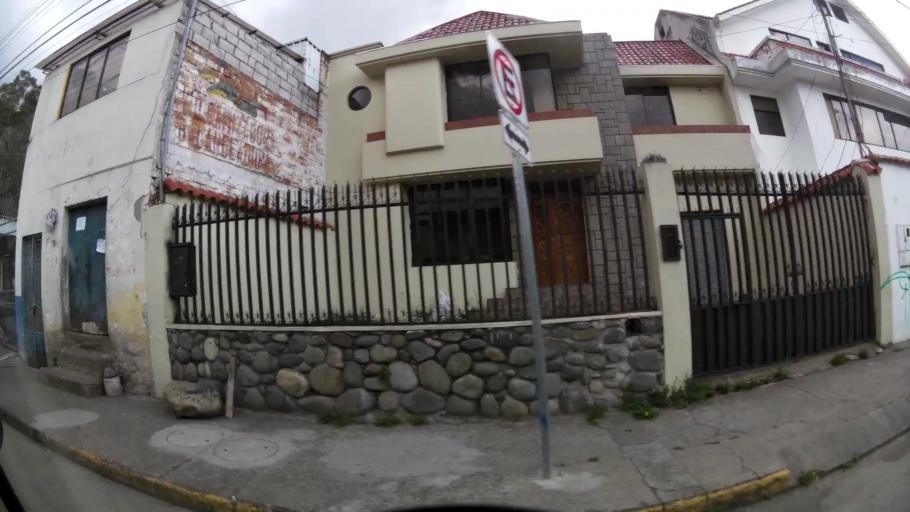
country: EC
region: Azuay
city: Cuenca
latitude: -2.8942
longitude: -79.0161
